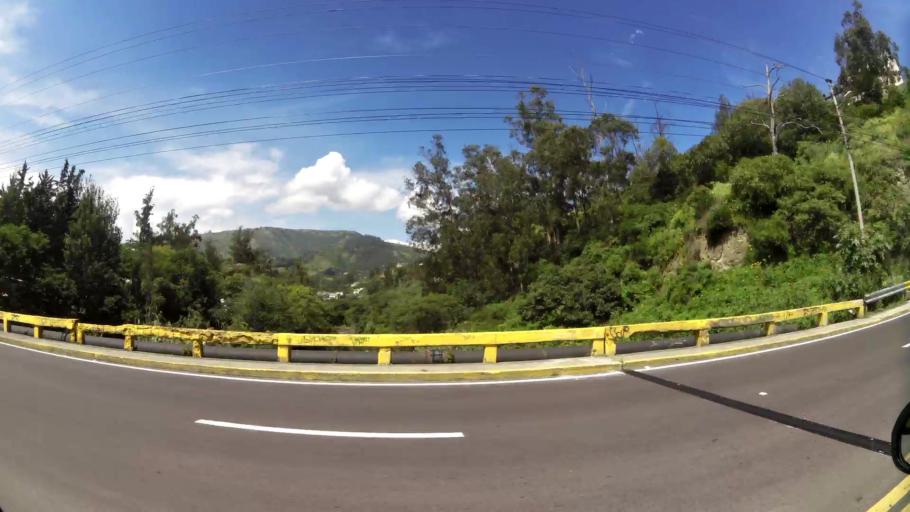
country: EC
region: Pichincha
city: Quito
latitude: -0.2115
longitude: -78.4236
